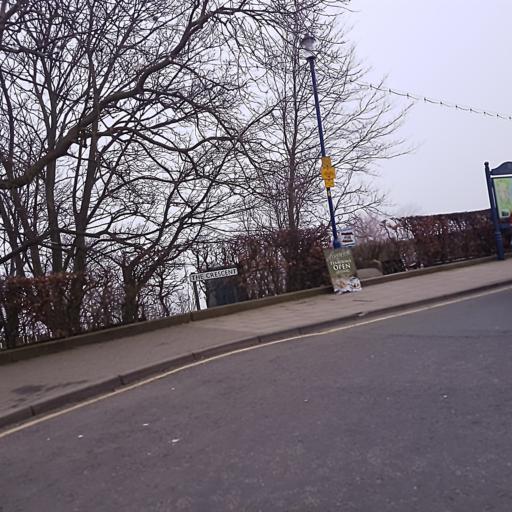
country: GB
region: England
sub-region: North Yorkshire
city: Filey
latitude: 54.2082
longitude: -0.2863
